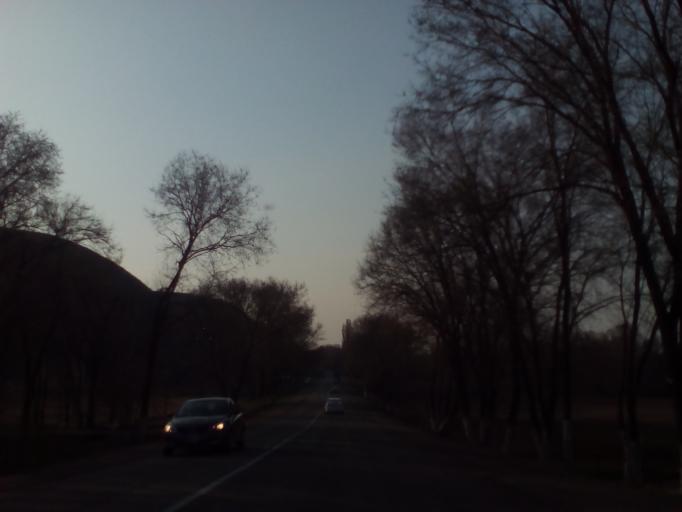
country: KZ
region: Almaty Oblysy
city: Burunday
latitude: 43.1669
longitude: 76.5437
